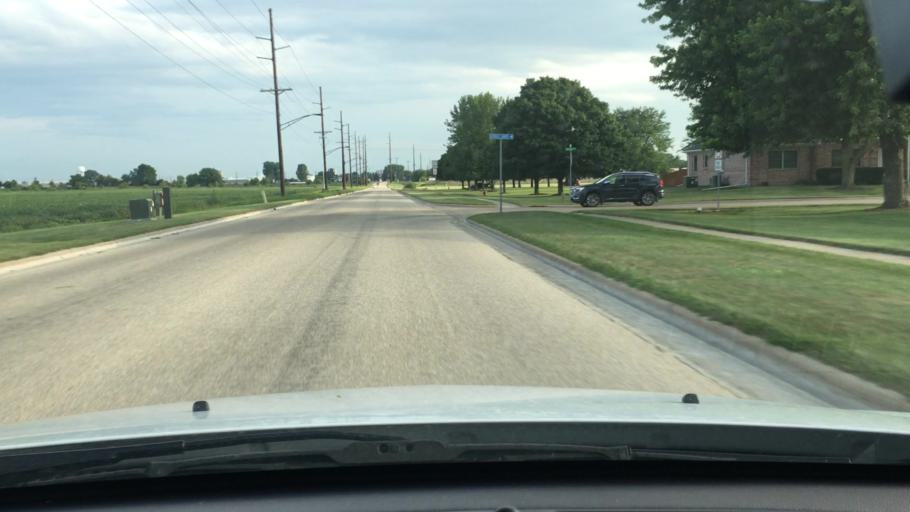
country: US
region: Illinois
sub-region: Ogle County
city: Rochelle
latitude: 41.9281
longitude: -89.0545
